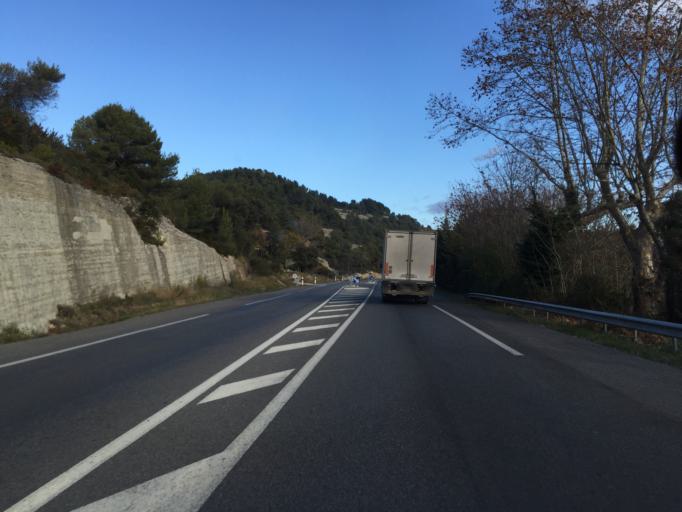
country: FR
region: Provence-Alpes-Cote d'Azur
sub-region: Departement du Vaucluse
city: Menerbes
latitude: 43.8593
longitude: 5.2123
